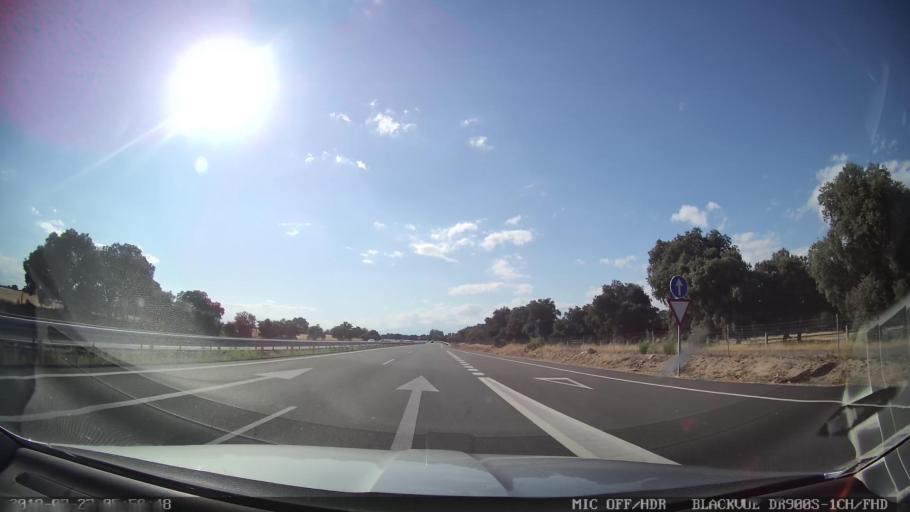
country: ES
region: Castille-La Mancha
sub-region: Province of Toledo
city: Alcanizo
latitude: 39.9204
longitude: -5.0836
